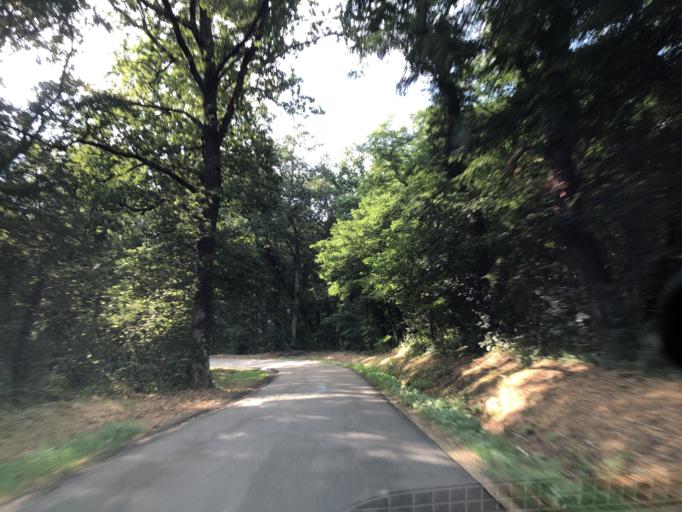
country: FR
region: Bourgogne
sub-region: Departement de l'Yonne
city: Charbuy
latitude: 47.8208
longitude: 3.4994
